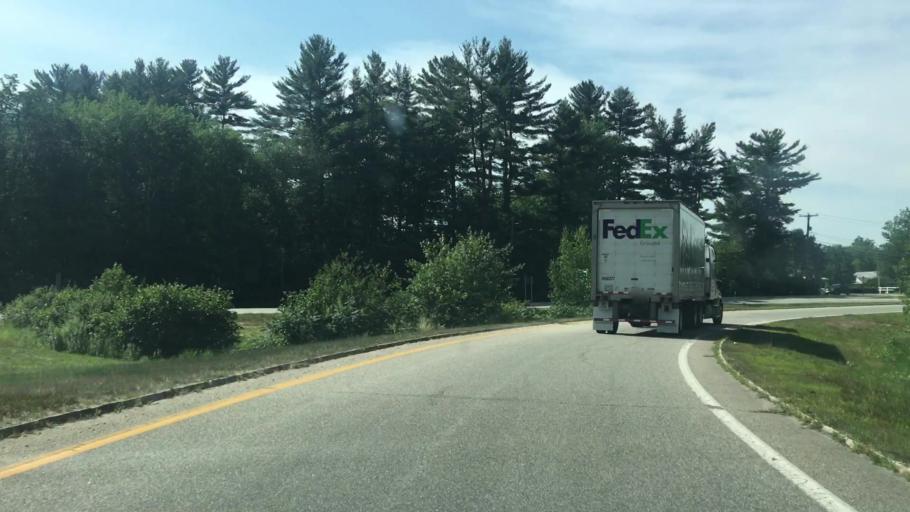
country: US
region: New Hampshire
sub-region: Strafford County
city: Rochester
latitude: 43.3316
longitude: -70.9740
